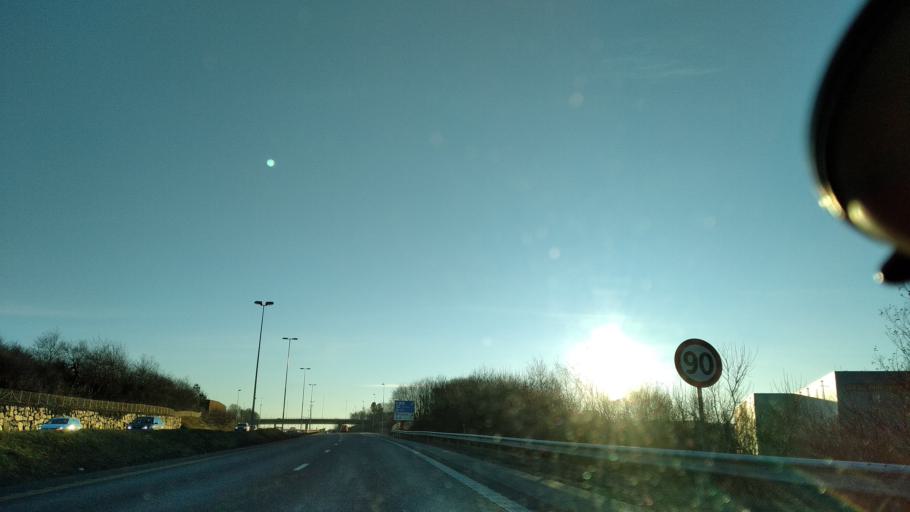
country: NO
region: Rogaland
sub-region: Sandnes
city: Sandnes
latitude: 58.8608
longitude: 5.7111
